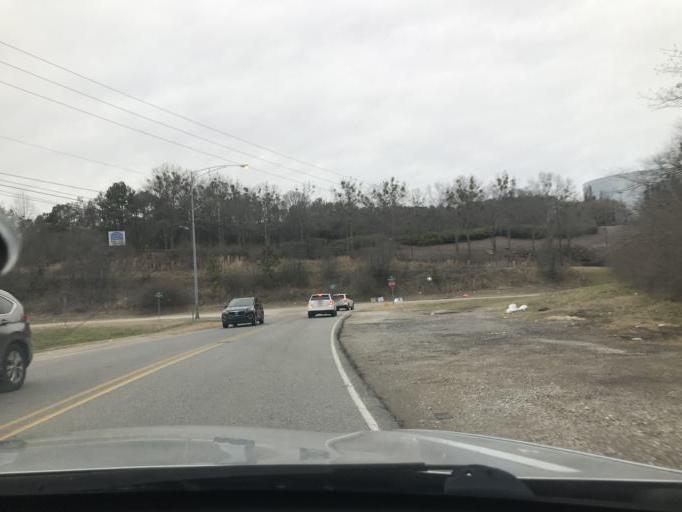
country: US
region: Alabama
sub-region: Jefferson County
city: Cahaba Heights
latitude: 33.4413
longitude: -86.7271
